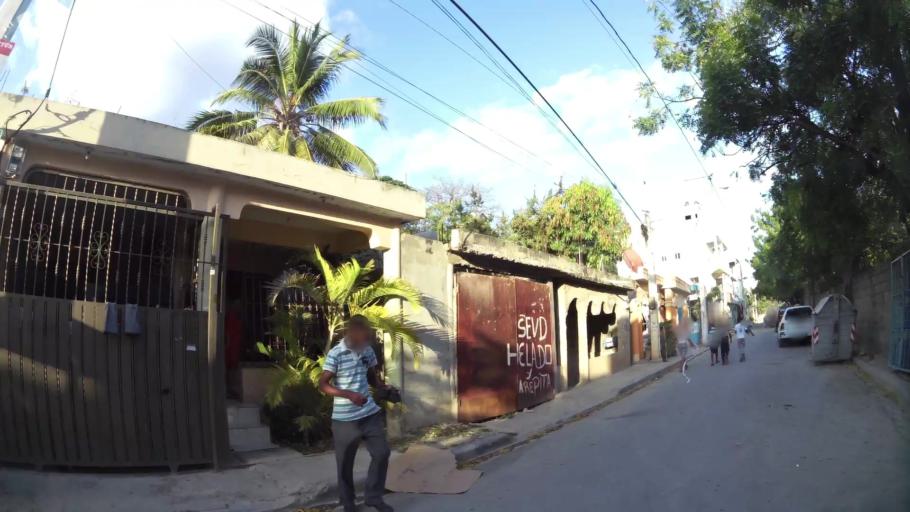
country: DO
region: Santo Domingo
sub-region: Santo Domingo
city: Santo Domingo Este
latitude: 18.4828
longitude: -69.8289
